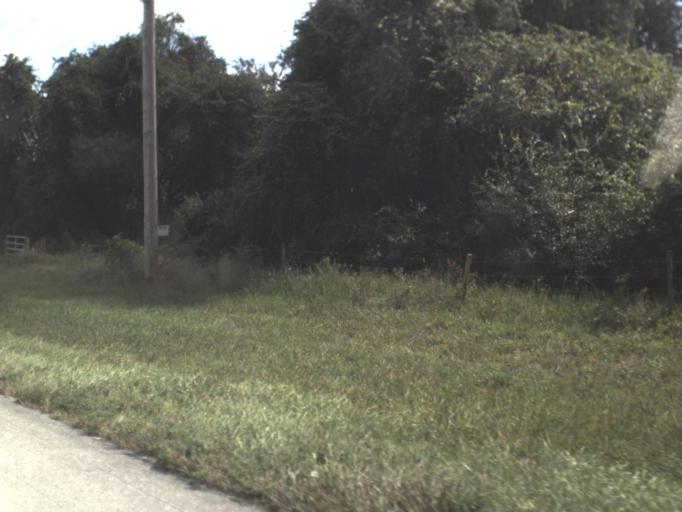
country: US
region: Florida
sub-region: Highlands County
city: Sebring
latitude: 27.4124
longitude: -81.5116
